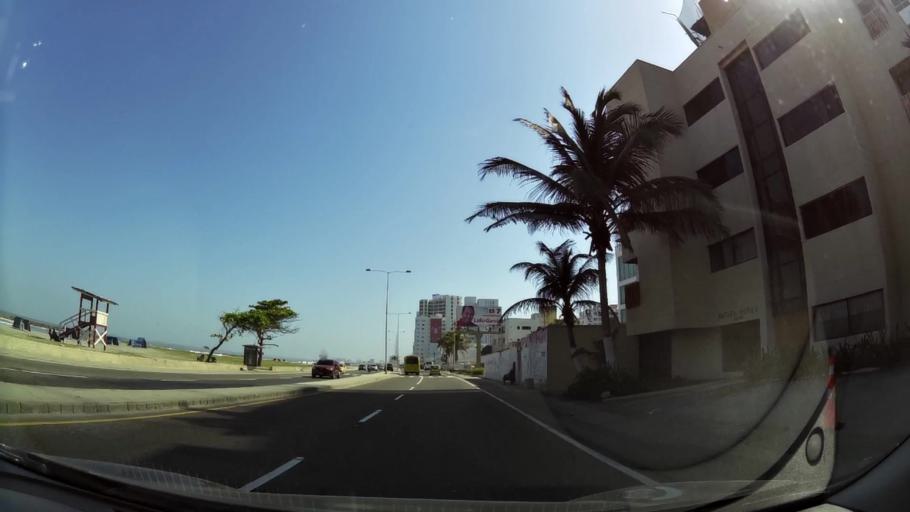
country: CO
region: Bolivar
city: Cartagena
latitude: 10.4338
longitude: -75.5409
